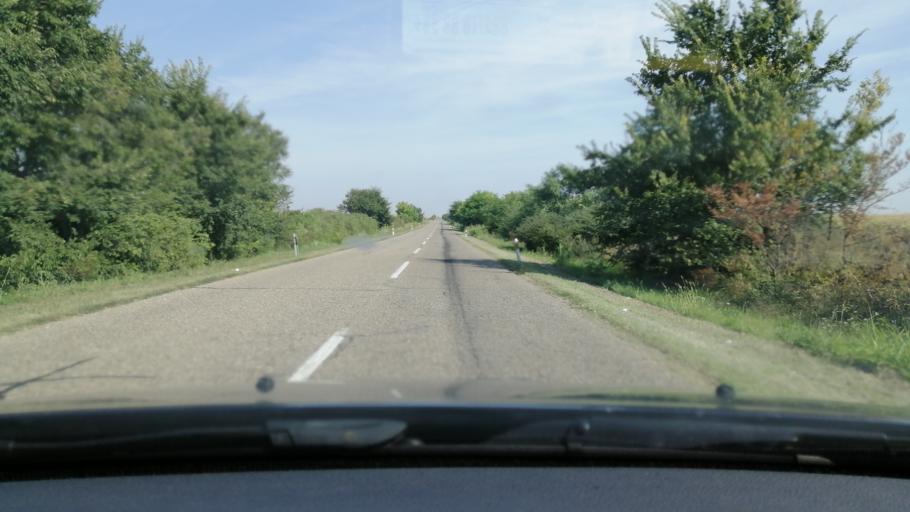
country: RS
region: Autonomna Pokrajina Vojvodina
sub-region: Juznobanatski Okrug
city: Kovacica
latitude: 45.1398
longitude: 20.6163
